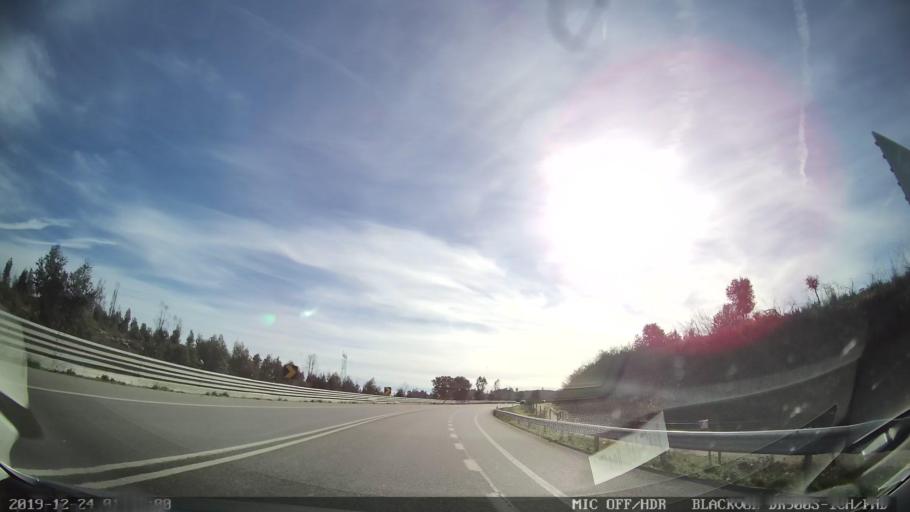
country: PT
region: Portalegre
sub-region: Nisa
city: Nisa
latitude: 39.5152
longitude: -7.7689
